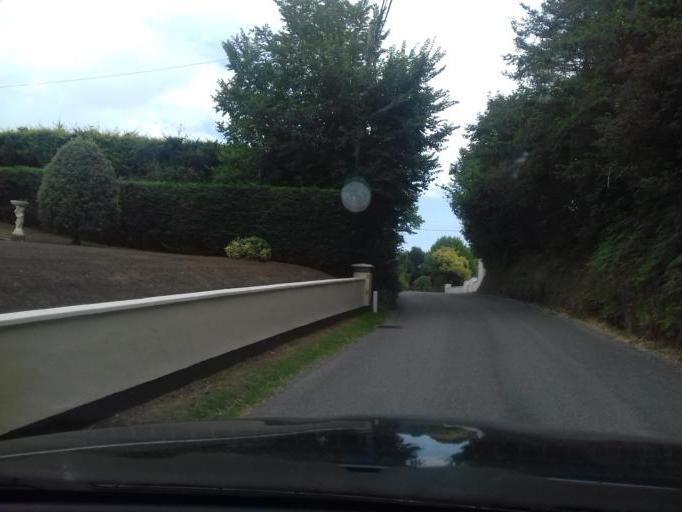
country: IE
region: Leinster
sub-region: Loch Garman
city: Castlebridge
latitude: 52.4006
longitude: -6.3992
